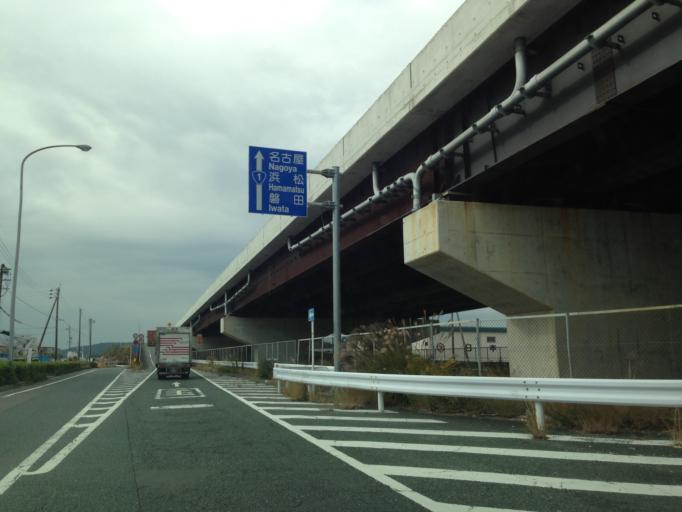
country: JP
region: Shizuoka
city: Fukuroi
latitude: 34.7518
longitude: 137.9060
